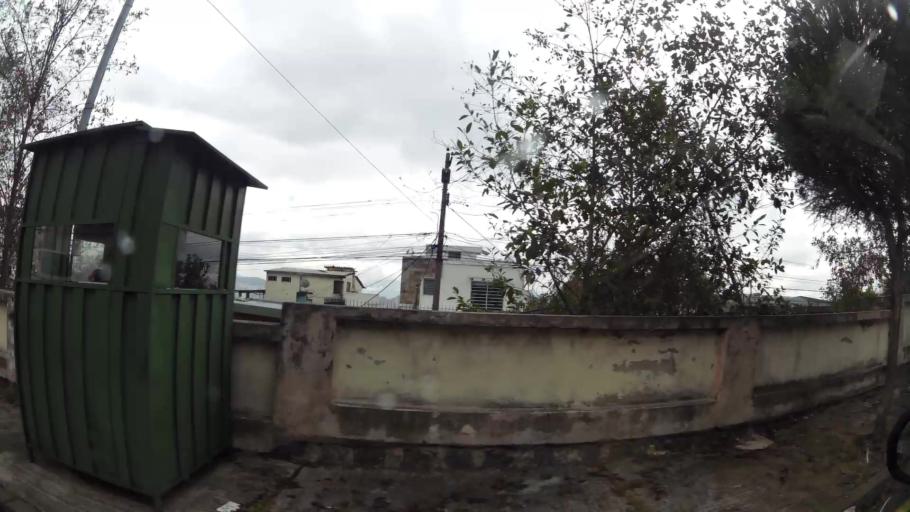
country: EC
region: Pichincha
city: Quito
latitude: -0.2034
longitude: -78.5093
